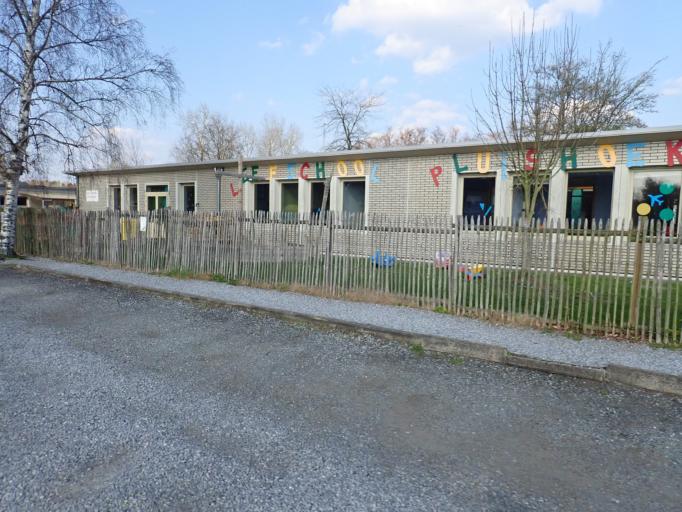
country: BE
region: Flanders
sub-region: Provincie Antwerpen
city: Heist-op-den-Berg
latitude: 51.0442
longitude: 4.7283
